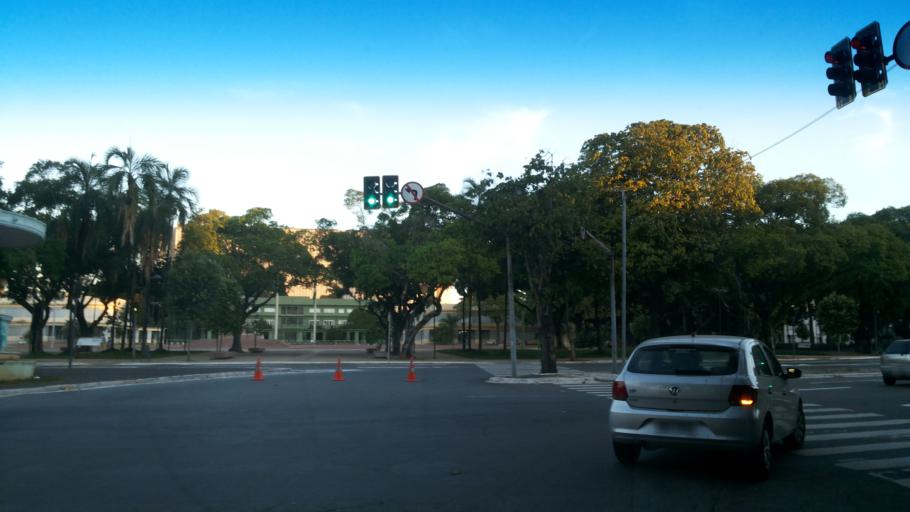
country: BR
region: Goias
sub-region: Goiania
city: Goiania
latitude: -16.6793
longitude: -49.2569
